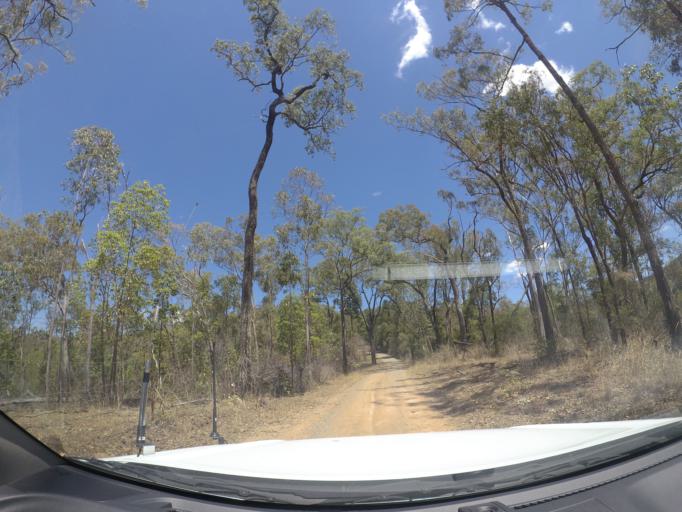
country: AU
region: Queensland
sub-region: Ipswich
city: Deebing Heights
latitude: -27.8298
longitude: 152.8285
